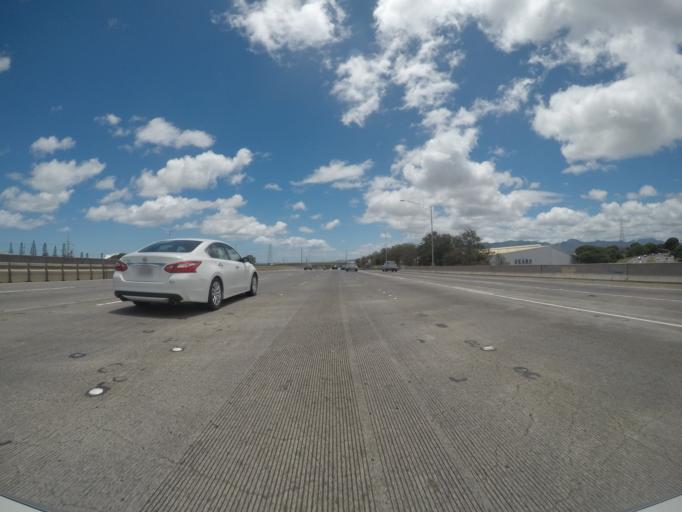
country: US
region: Hawaii
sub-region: Honolulu County
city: Pearl City, Manana
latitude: 21.3925
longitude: -157.9592
